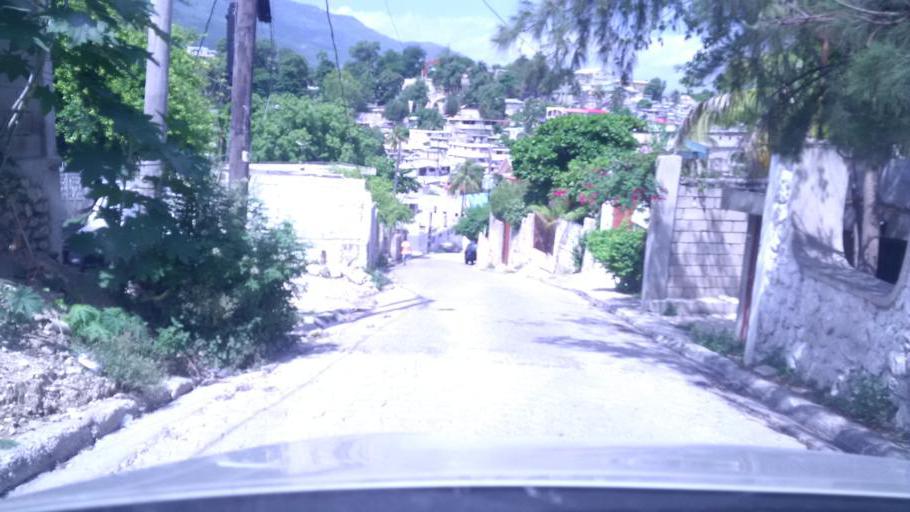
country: HT
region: Ouest
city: Delmas 73
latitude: 18.5423
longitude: -72.3164
